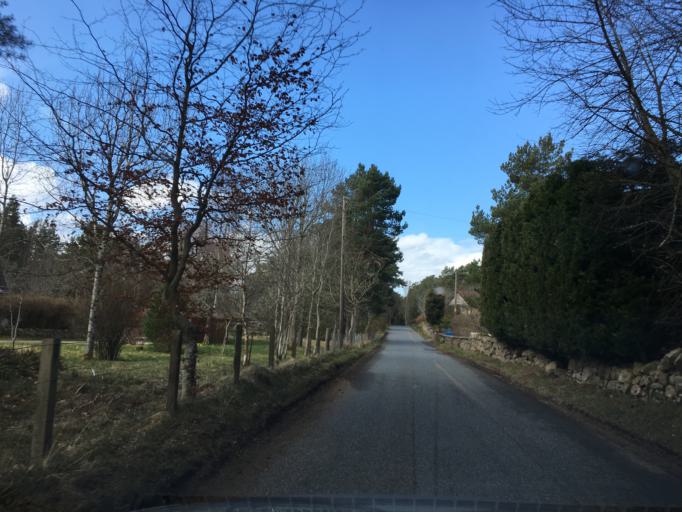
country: GB
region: Scotland
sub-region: Highland
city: Aviemore
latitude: 57.1760
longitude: -3.7954
